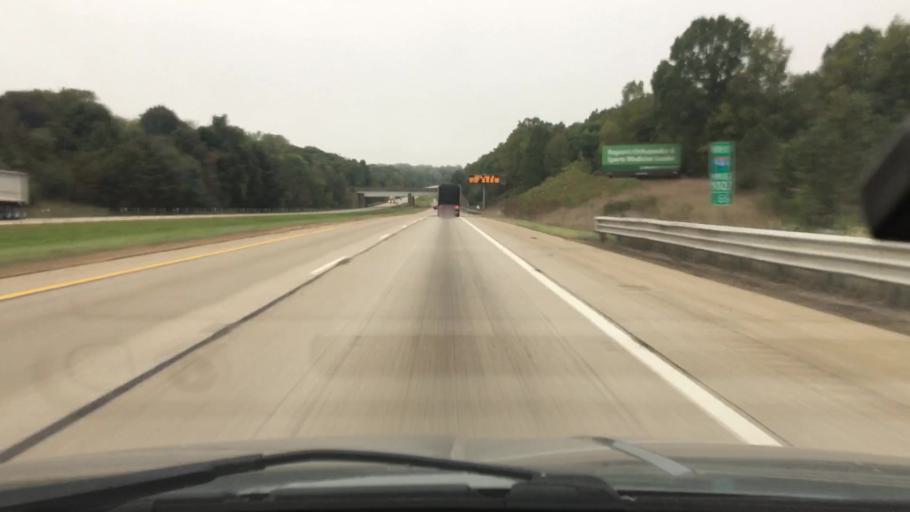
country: US
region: Michigan
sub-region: Calhoun County
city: Brownlee Park
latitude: 42.2938
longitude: -85.1038
